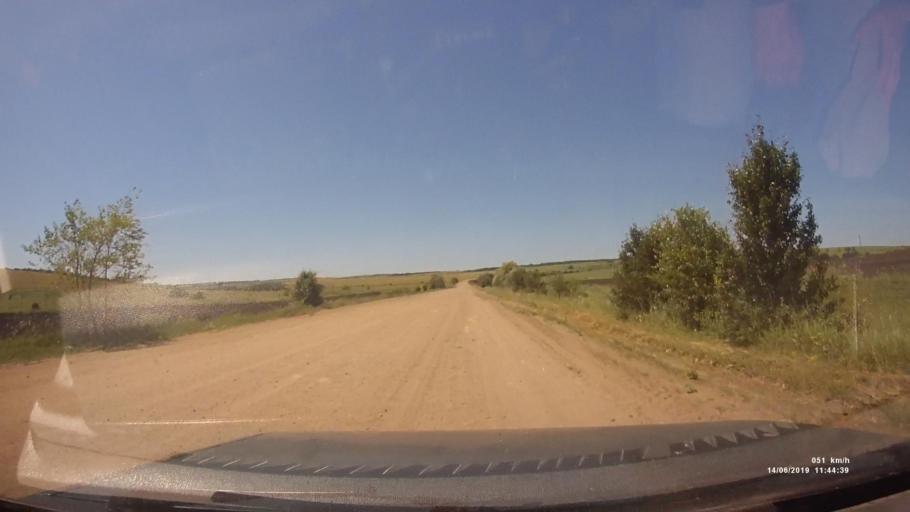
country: RU
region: Rostov
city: Kazanskaya
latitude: 49.8537
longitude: 41.3216
